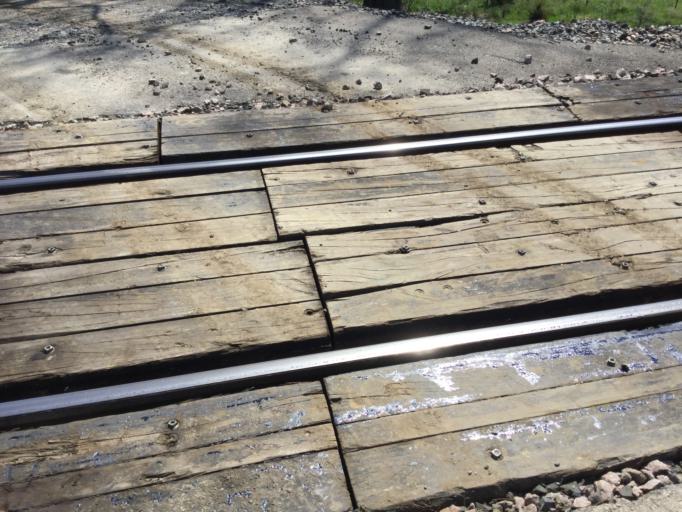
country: US
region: Kansas
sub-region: Neosho County
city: Erie
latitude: 37.4713
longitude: -95.2434
